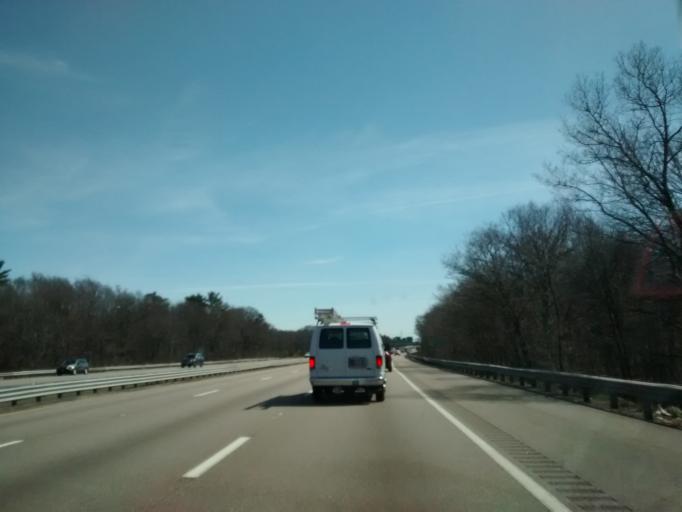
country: US
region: Massachusetts
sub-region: Norfolk County
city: Randolph
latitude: 42.1629
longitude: -71.0705
